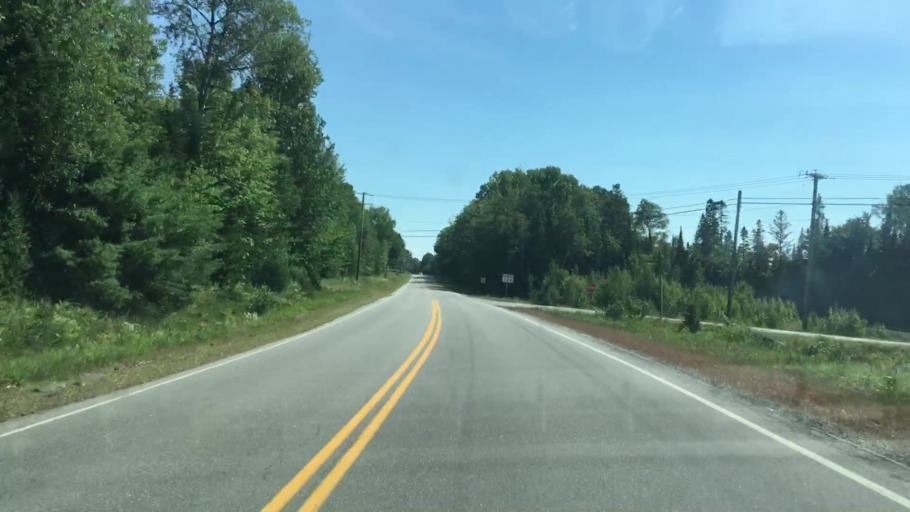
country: US
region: Maine
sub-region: Piscataquis County
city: Milo
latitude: 45.1997
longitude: -68.9062
